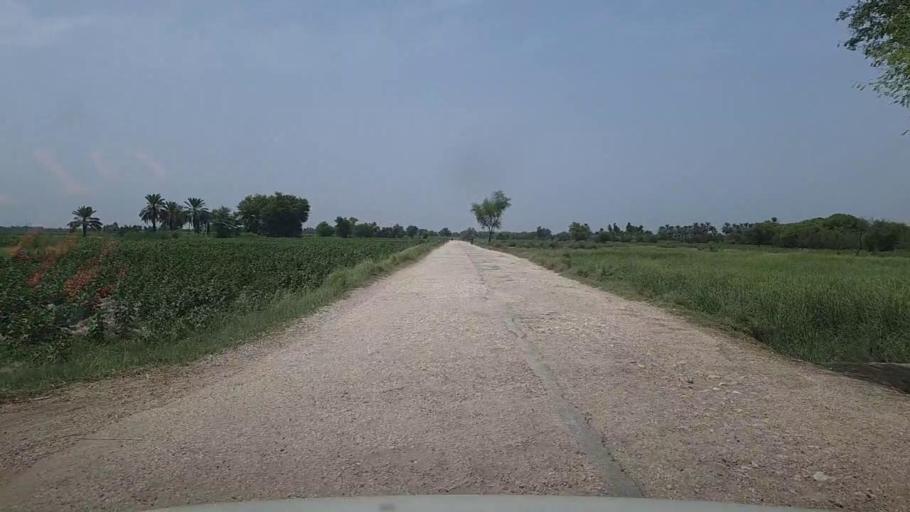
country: PK
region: Sindh
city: Pano Aqil
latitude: 27.8451
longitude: 69.1494
